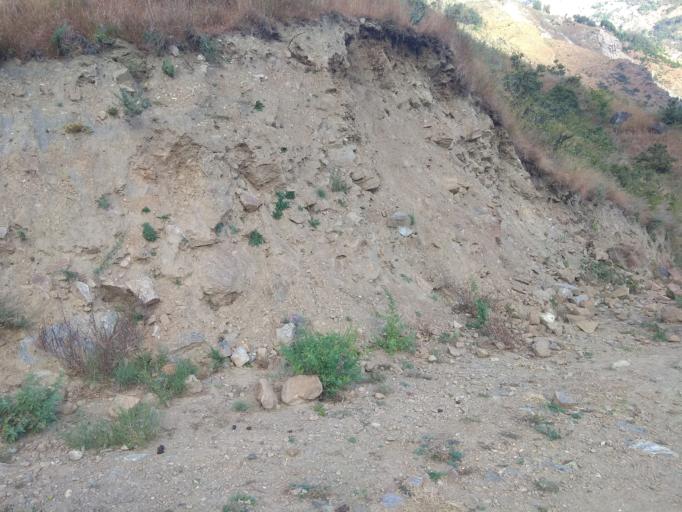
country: NP
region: Mid Western
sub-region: Bheri Zone
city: Dailekh
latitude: 29.2301
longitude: 81.6510
